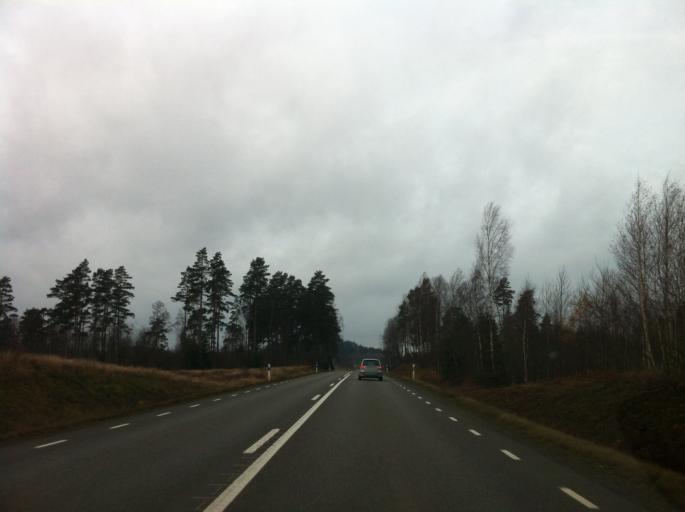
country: SE
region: Joenkoeping
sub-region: Vetlanda Kommun
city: Landsbro
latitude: 57.4017
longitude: 14.9284
